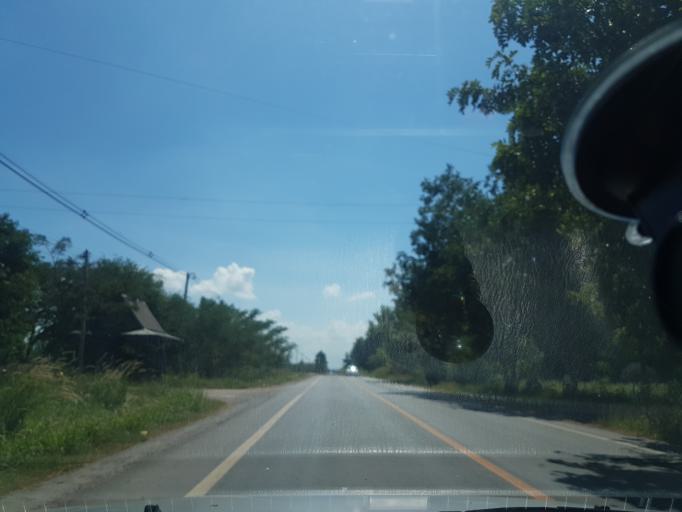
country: TH
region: Lop Buri
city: Phatthana Nikhom
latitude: 14.9681
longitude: 101.0066
